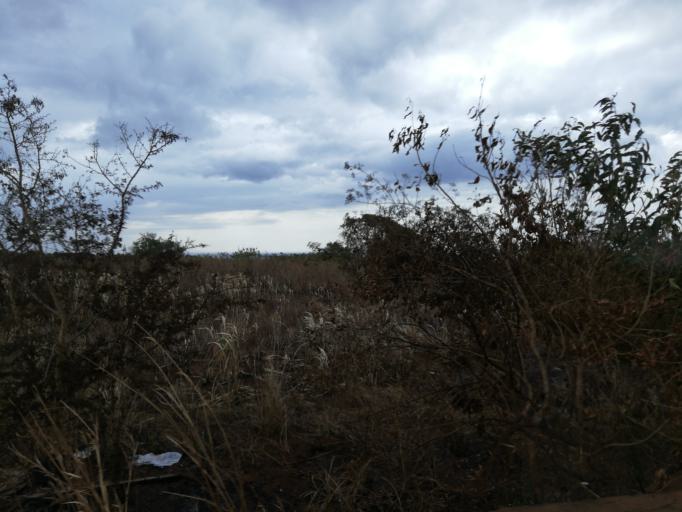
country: MU
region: Black River
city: Petite Riviere
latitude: -20.2068
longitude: 57.4580
